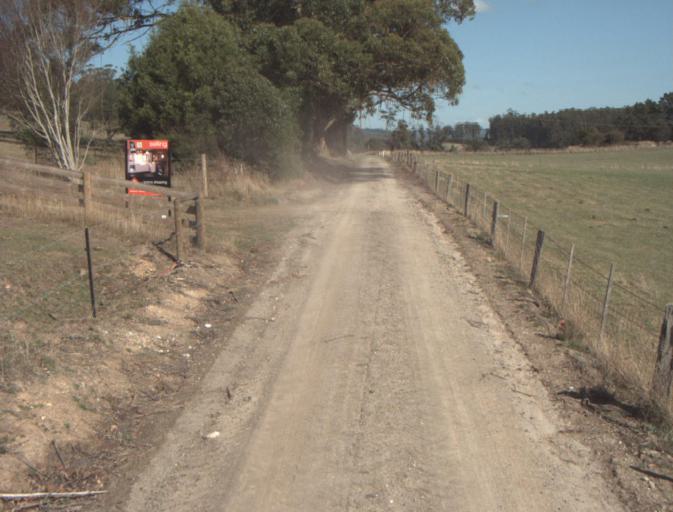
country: AU
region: Tasmania
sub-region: Launceston
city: Mayfield
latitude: -41.2203
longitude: 147.2392
